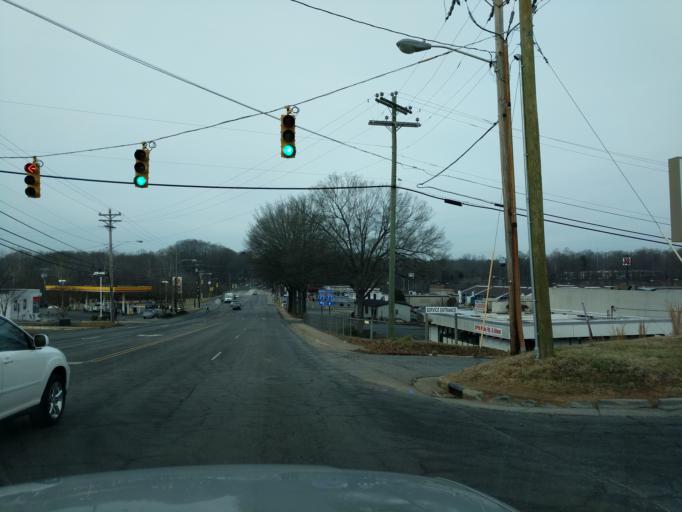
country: US
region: North Carolina
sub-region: Iredell County
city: Statesville
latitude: 35.7909
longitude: -80.8592
